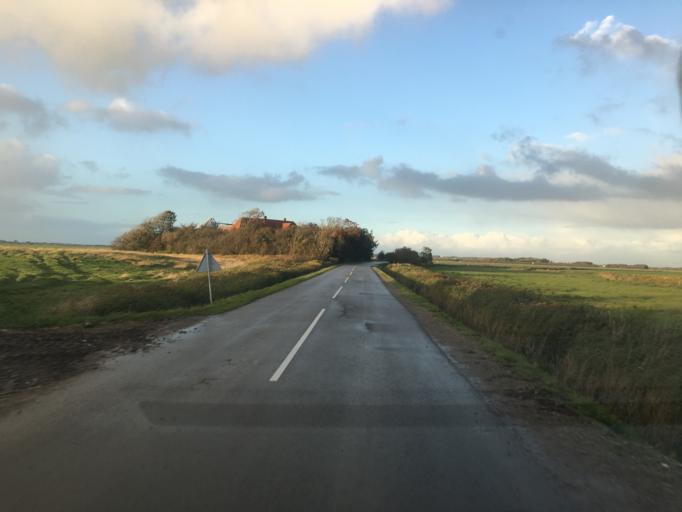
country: DE
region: Schleswig-Holstein
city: Aventoft
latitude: 54.9115
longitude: 8.7699
